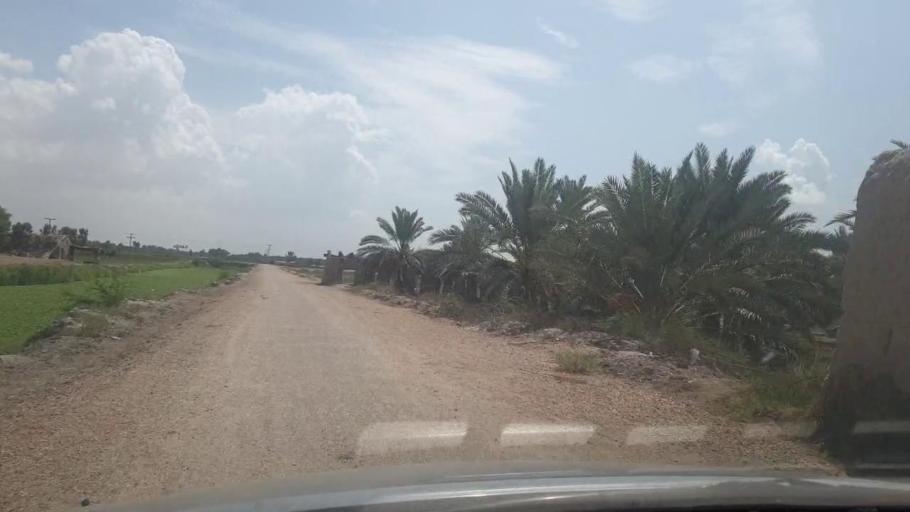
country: PK
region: Sindh
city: Khairpur
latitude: 27.4833
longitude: 68.8134
